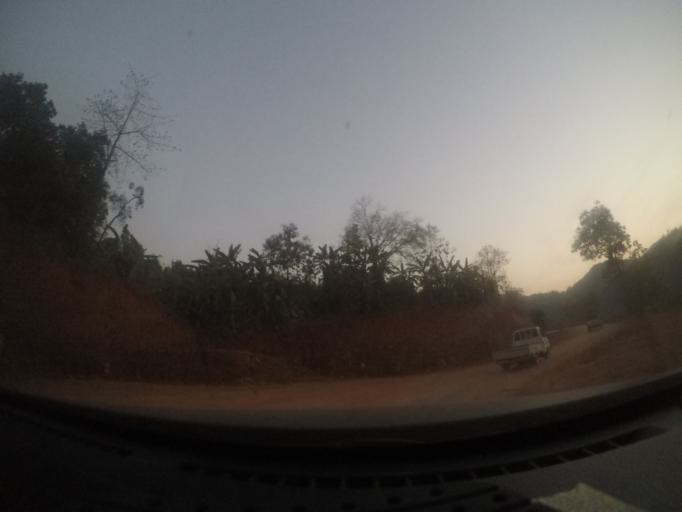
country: MM
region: Mandalay
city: Yamethin
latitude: 20.6950
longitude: 96.5045
